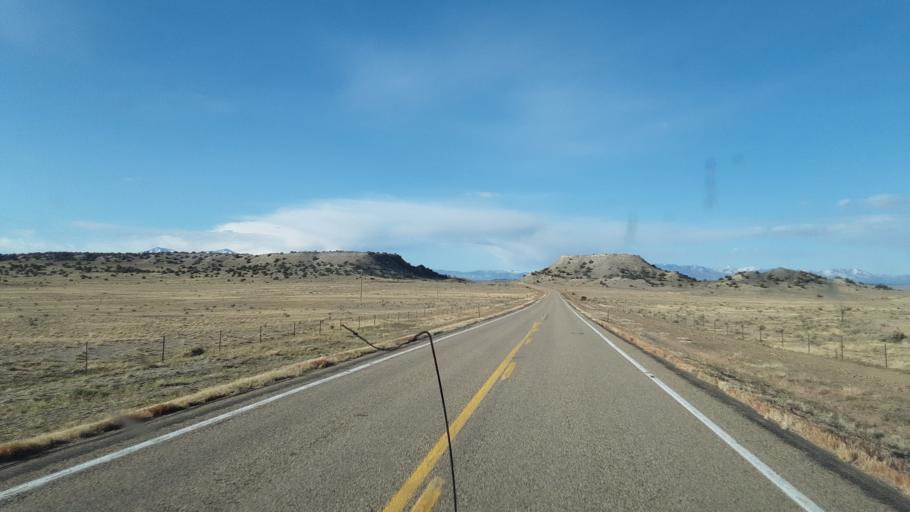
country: US
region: Colorado
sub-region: Huerfano County
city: Walsenburg
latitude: 37.6962
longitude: -104.6208
